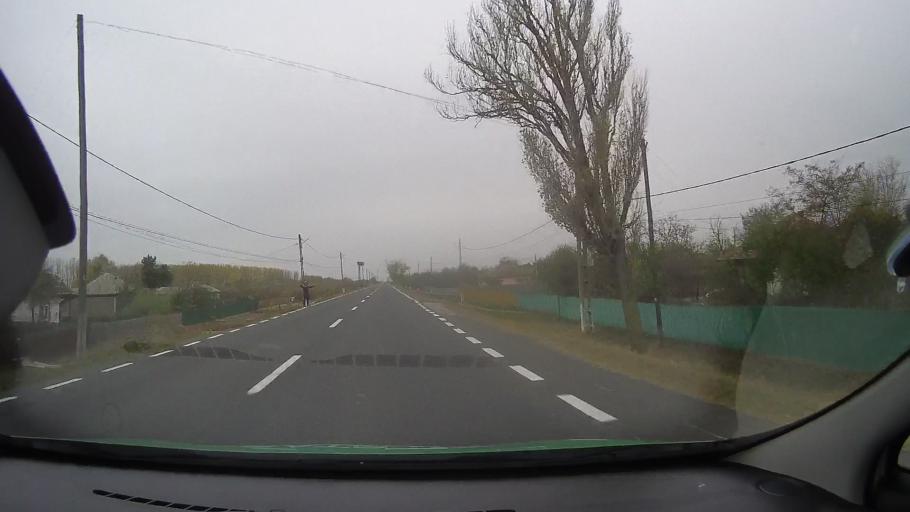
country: RO
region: Ialomita
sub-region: Comuna Giurgeni
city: Giurgeni
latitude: 44.7382
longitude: 27.8555
